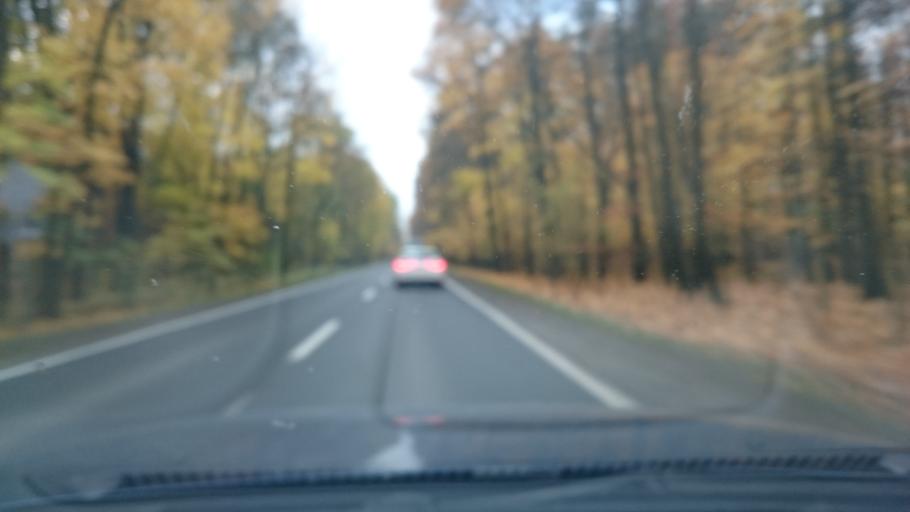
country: PL
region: Silesian Voivodeship
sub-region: Powiat rybnicki
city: Ksiazenice
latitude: 50.1143
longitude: 18.5895
